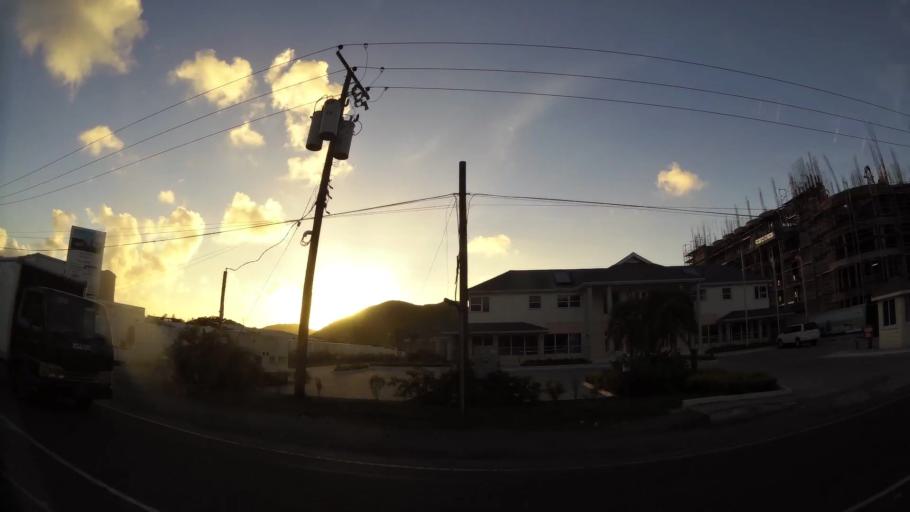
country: LC
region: Gros-Islet
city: Gros Islet
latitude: 14.0724
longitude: -60.9473
